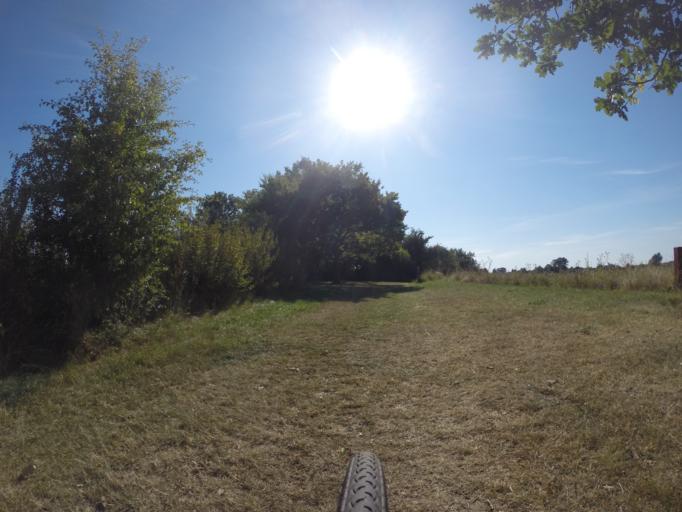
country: DK
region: Capital Region
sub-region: Herlev Kommune
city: Herlev
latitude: 55.7483
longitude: 12.4332
